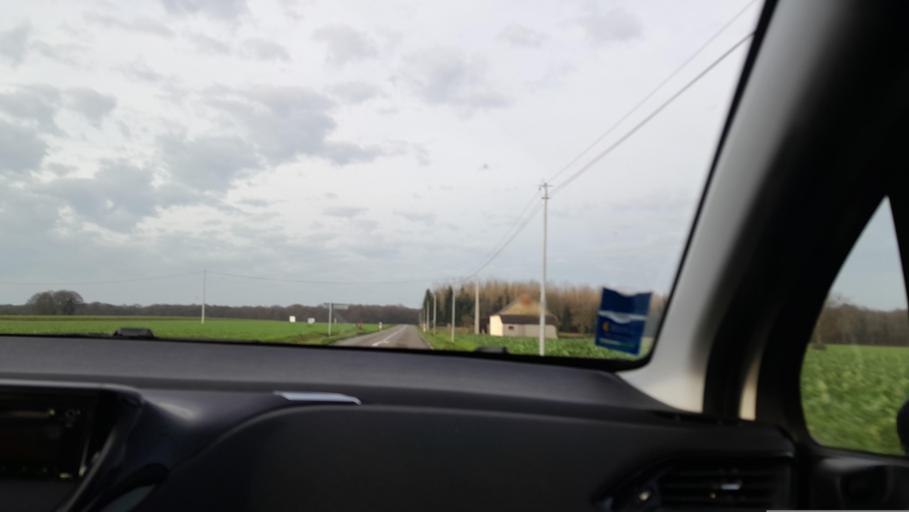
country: FR
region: Brittany
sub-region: Departement d'Ille-et-Vilaine
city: La Guerche-de-Bretagne
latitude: 47.9016
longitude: -1.1706
